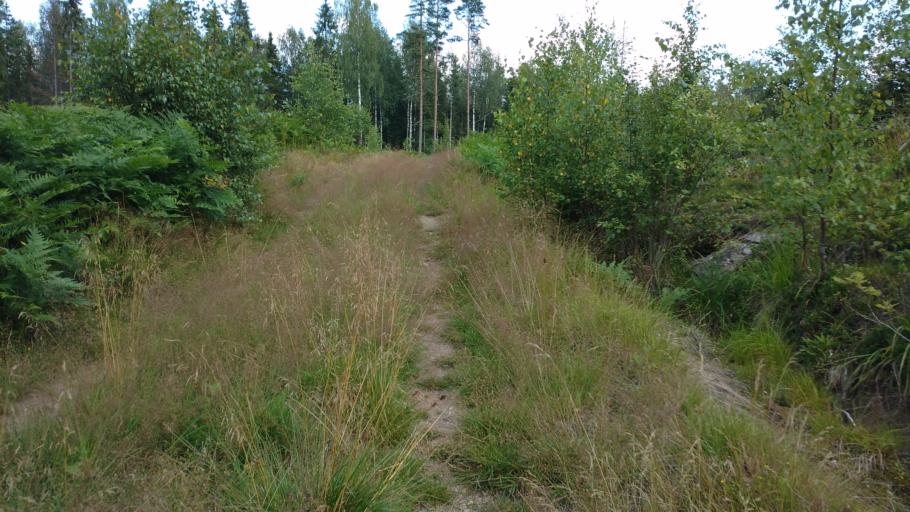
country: FI
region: Varsinais-Suomi
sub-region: Salo
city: Pertteli
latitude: 60.3948
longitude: 23.2298
